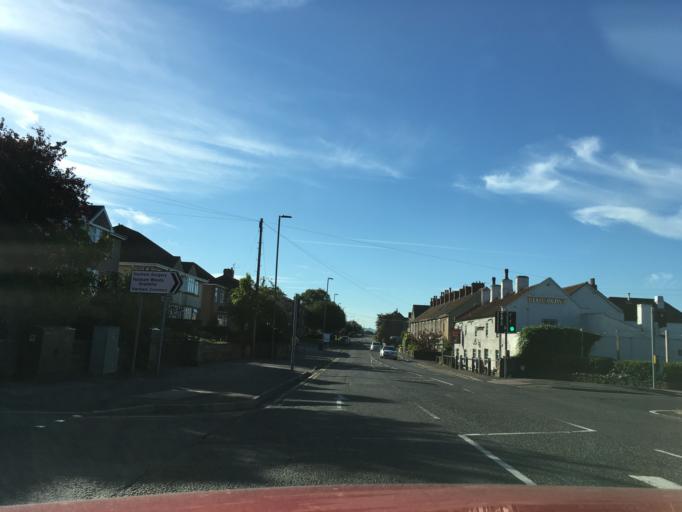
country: GB
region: England
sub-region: South Gloucestershire
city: Kingswood
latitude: 51.4466
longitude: -2.5092
